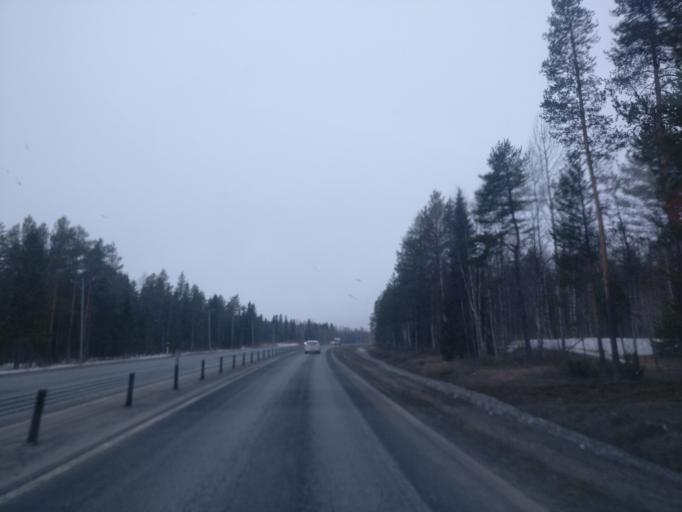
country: FI
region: Lapland
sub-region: Kemi-Tornio
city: Simo
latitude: 65.6685
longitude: 24.9399
